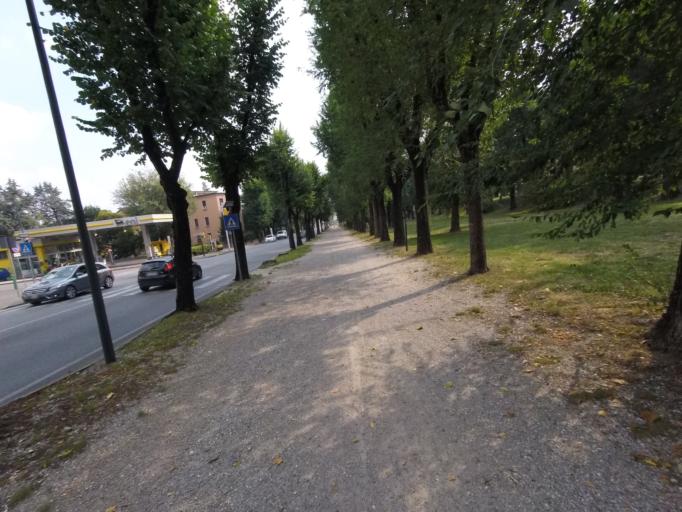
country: IT
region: Lombardy
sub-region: Provincia di Brescia
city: Brescia
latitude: 45.5397
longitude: 10.2316
